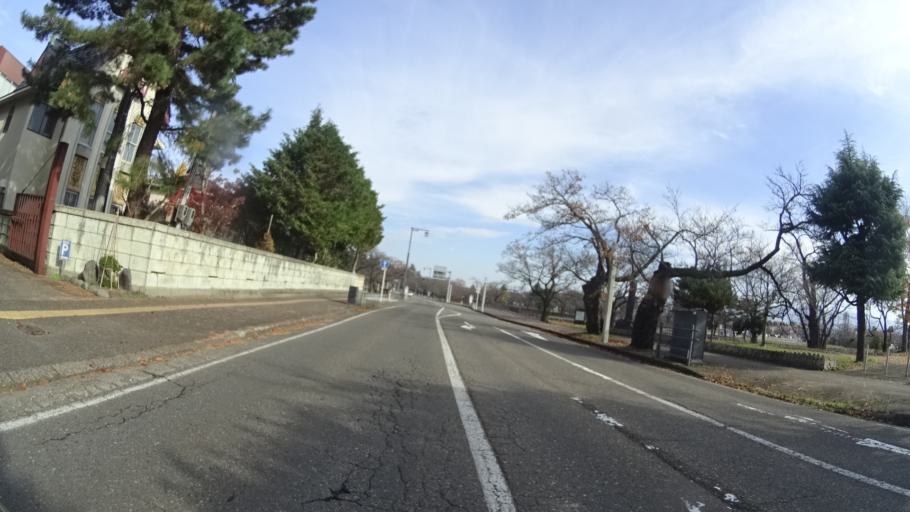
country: JP
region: Niigata
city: Joetsu
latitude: 37.1088
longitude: 138.2504
